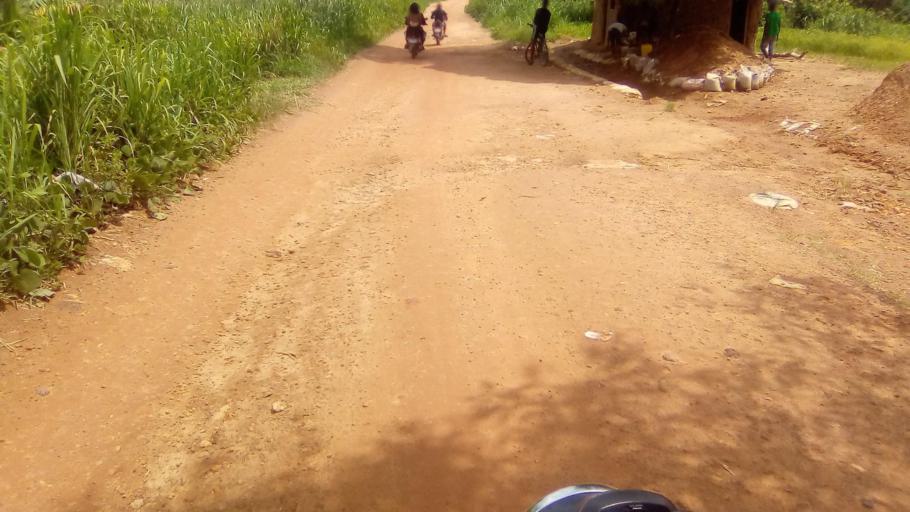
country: SL
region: Southern Province
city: Bo
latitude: 7.9764
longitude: -11.7668
